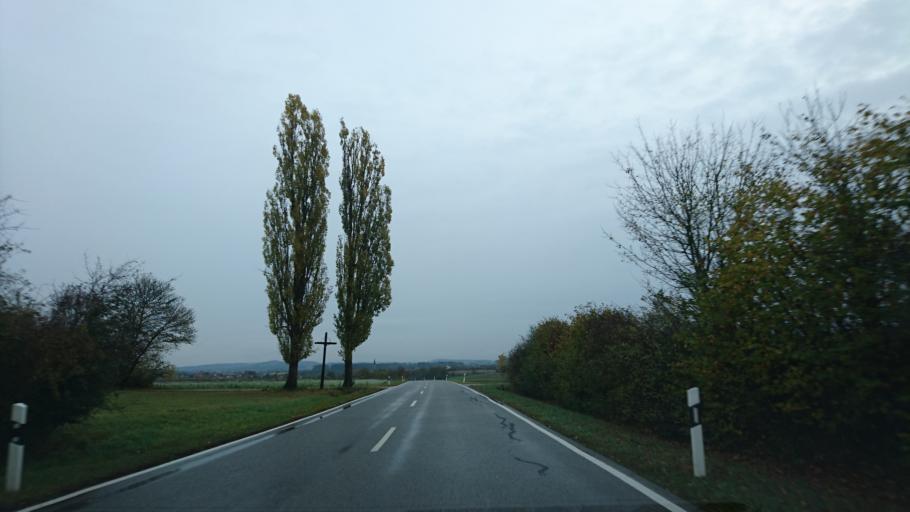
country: DE
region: Bavaria
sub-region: Regierungsbezirk Mittelfranken
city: Bergen
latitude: 49.0984
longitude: 11.1156
